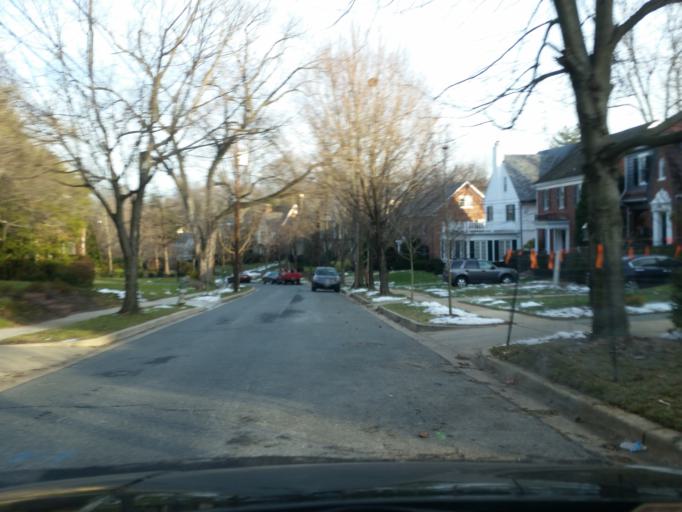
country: US
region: Maryland
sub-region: Montgomery County
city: Chevy Chase
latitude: 38.9846
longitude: -77.0767
